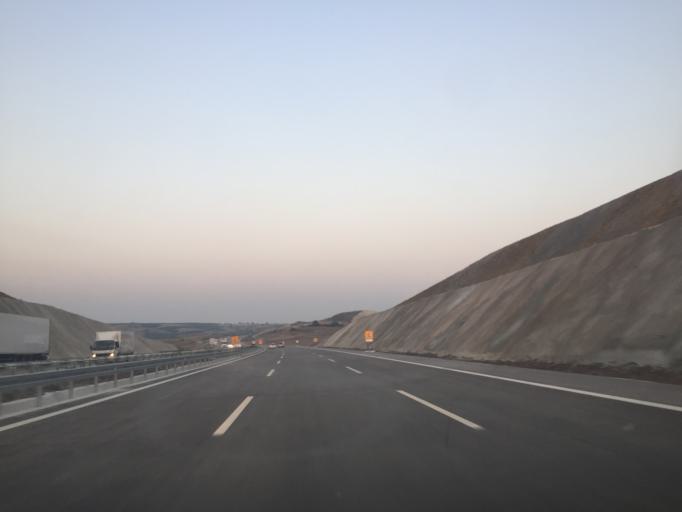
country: TR
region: Bursa
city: Mahmudiye
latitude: 40.2653
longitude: 28.6478
